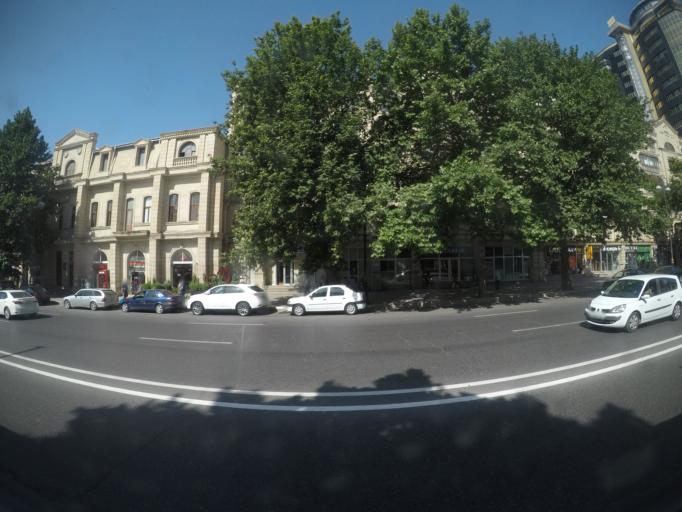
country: AZ
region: Baki
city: Badamdar
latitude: 40.3773
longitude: 49.8321
